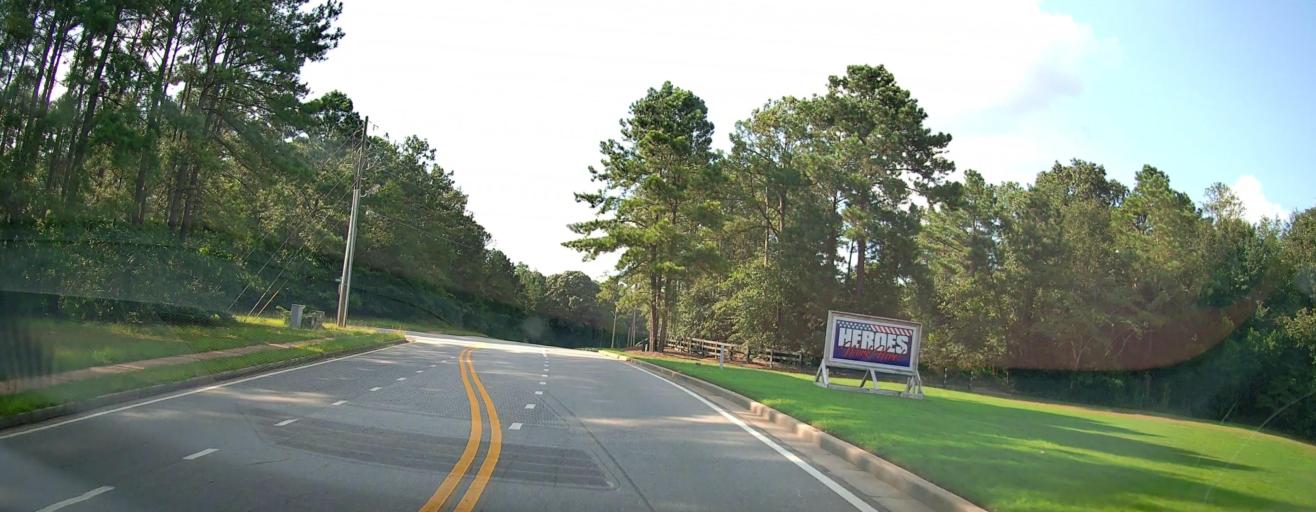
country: US
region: Georgia
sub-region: Houston County
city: Warner Robins
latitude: 32.5868
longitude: -83.6364
